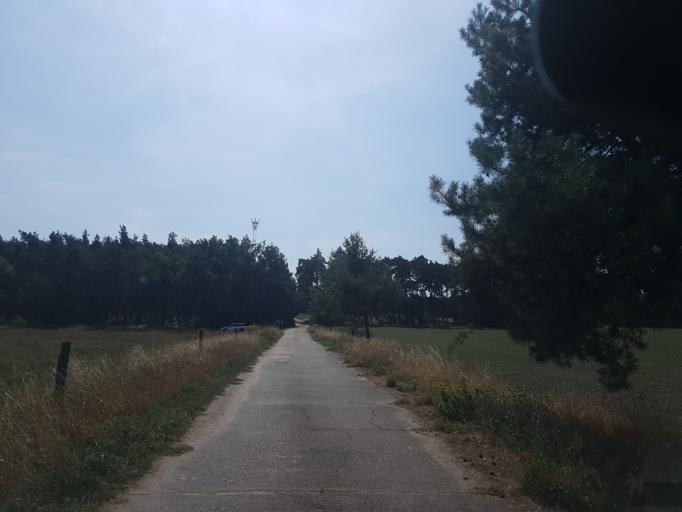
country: DE
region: Brandenburg
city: Treuenbrietzen
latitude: 52.0840
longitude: 12.8464
